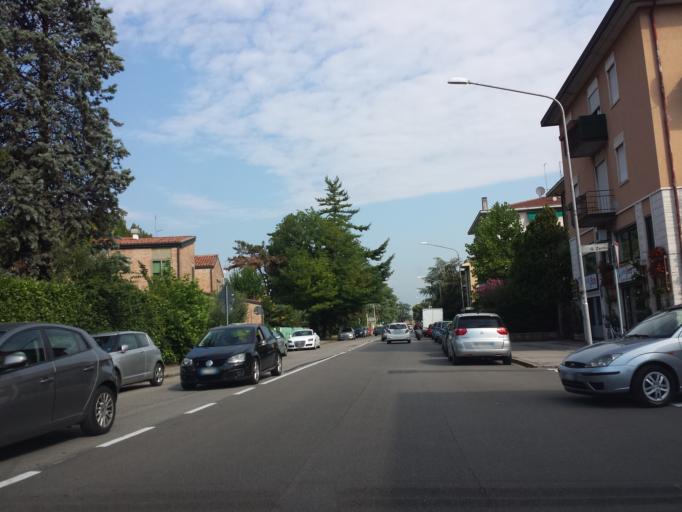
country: IT
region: Veneto
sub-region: Provincia di Vicenza
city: Vicenza
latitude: 45.5541
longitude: 11.5225
